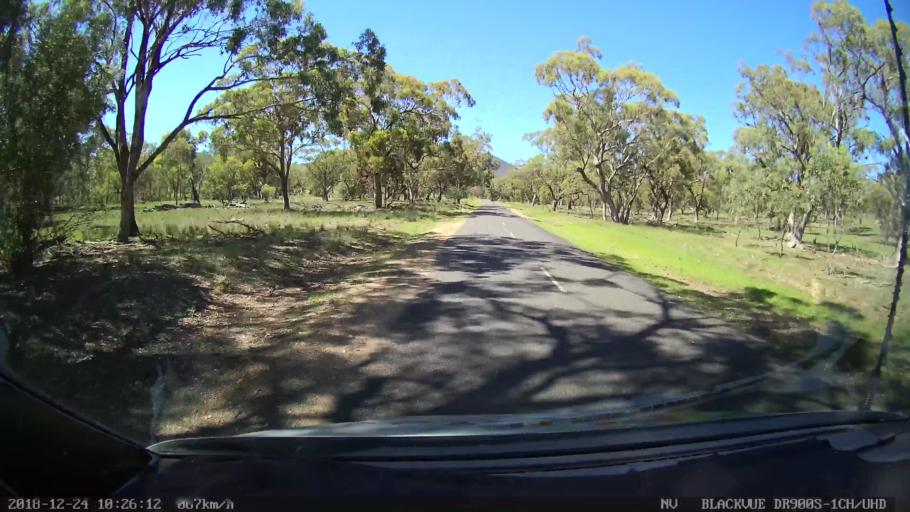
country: AU
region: New South Wales
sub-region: Liverpool Plains
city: Quirindi
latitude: -31.8070
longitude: 150.5279
